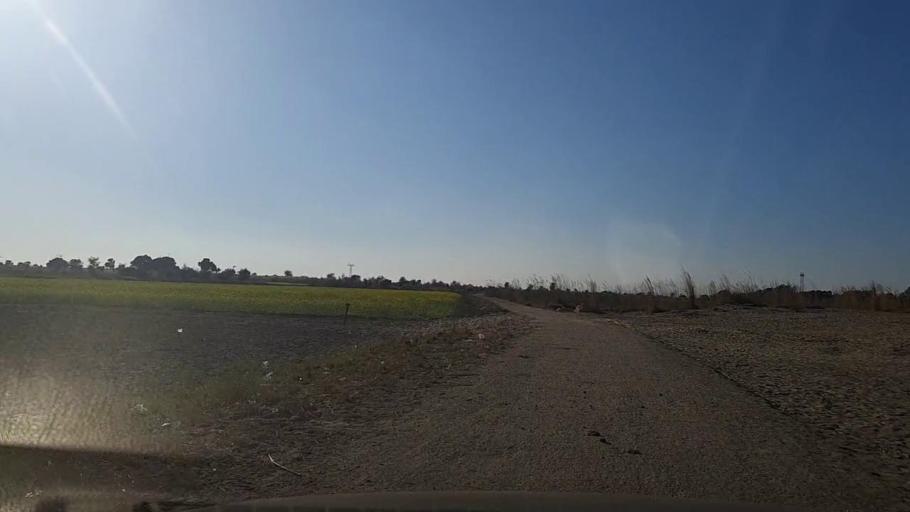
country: PK
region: Sindh
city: Khadro
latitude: 26.2471
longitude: 68.8629
